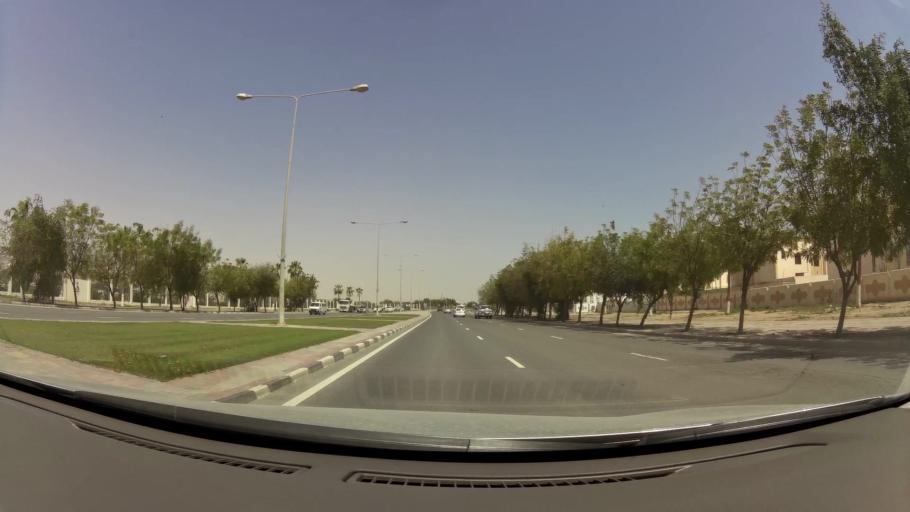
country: QA
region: Baladiyat ad Dawhah
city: Doha
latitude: 25.3628
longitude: 51.4952
